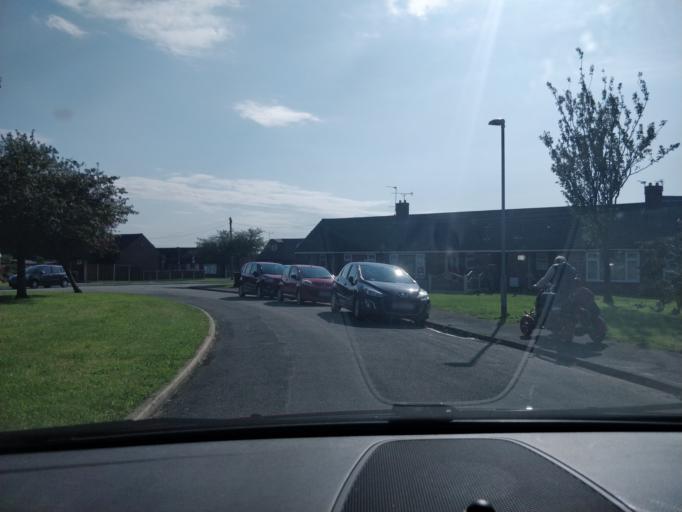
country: GB
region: England
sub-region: Lancashire
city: Banks
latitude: 53.6791
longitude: -2.9220
